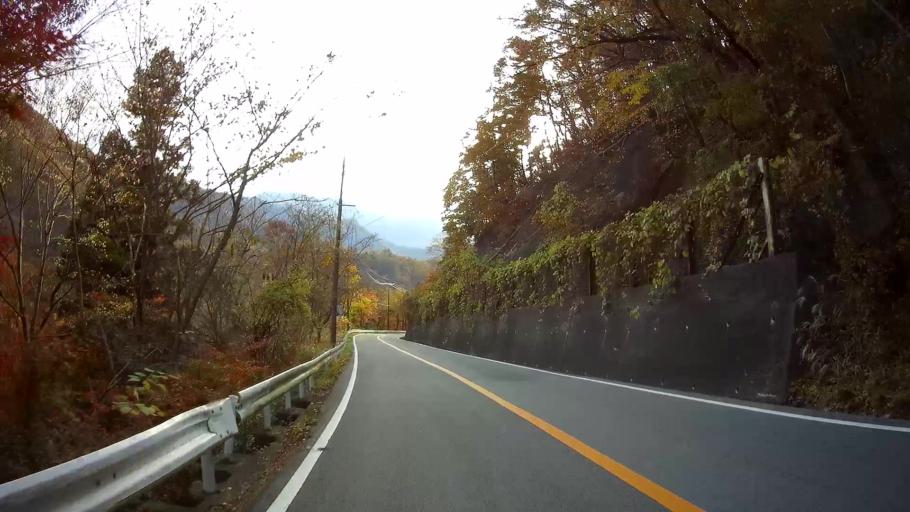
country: JP
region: Yamanashi
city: Fujikawaguchiko
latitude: 35.4780
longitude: 138.5545
